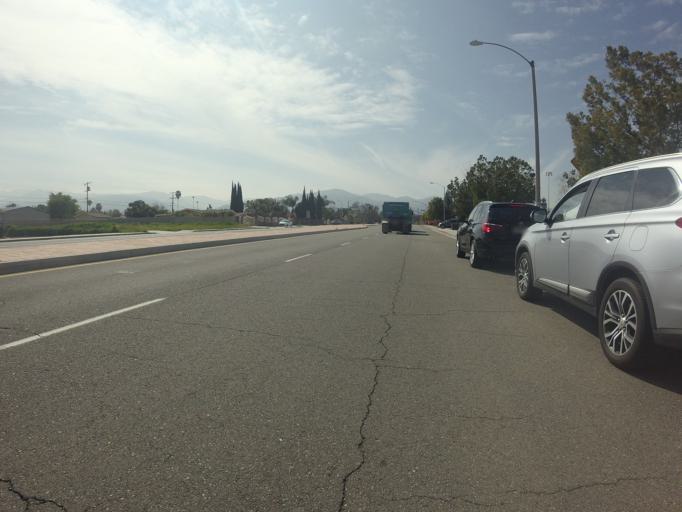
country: US
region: California
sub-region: Riverside County
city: El Cerrito
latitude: 33.8340
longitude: -117.5264
